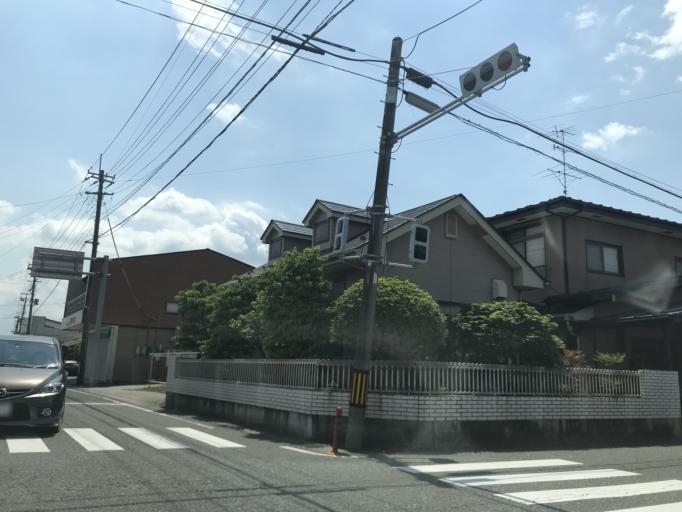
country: JP
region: Miyagi
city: Kogota
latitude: 38.5988
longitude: 141.0259
